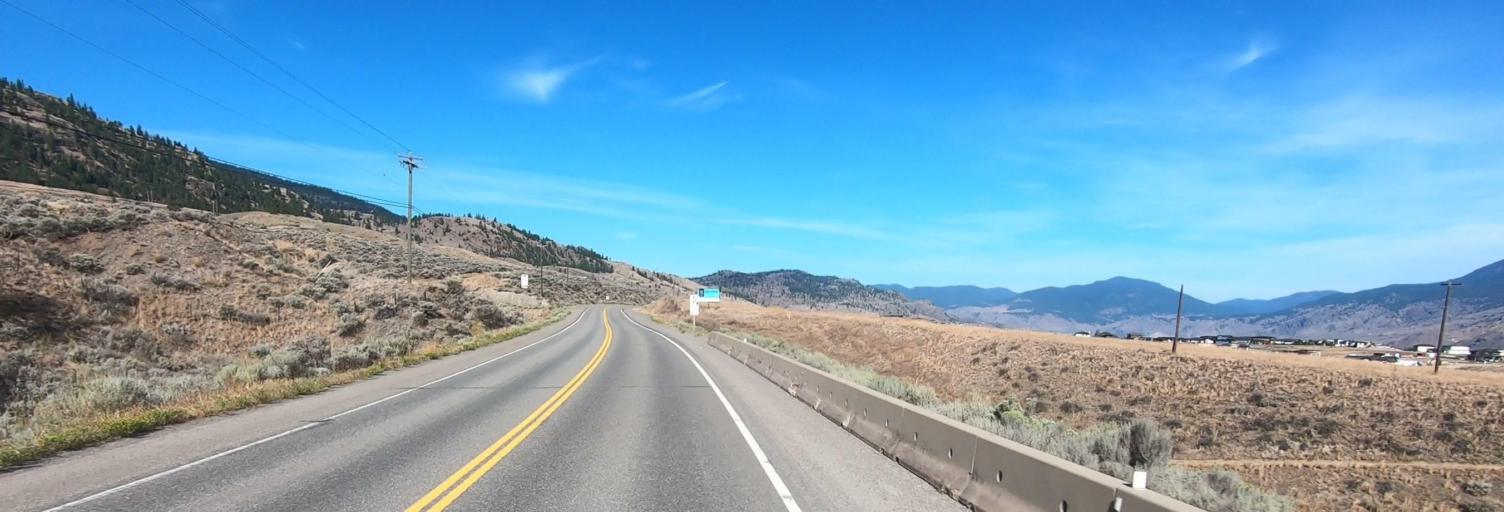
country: CA
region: British Columbia
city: Logan Lake
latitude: 50.7235
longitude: -120.6678
